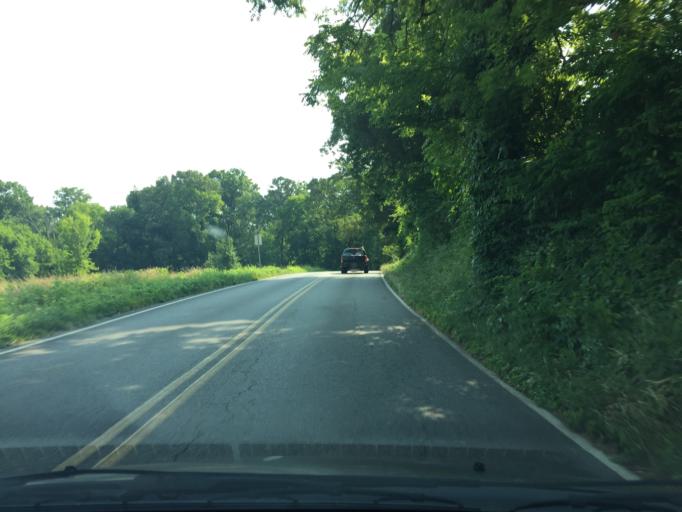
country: US
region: Tennessee
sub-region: Hamilton County
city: Middle Valley
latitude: 35.1749
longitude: -85.1609
